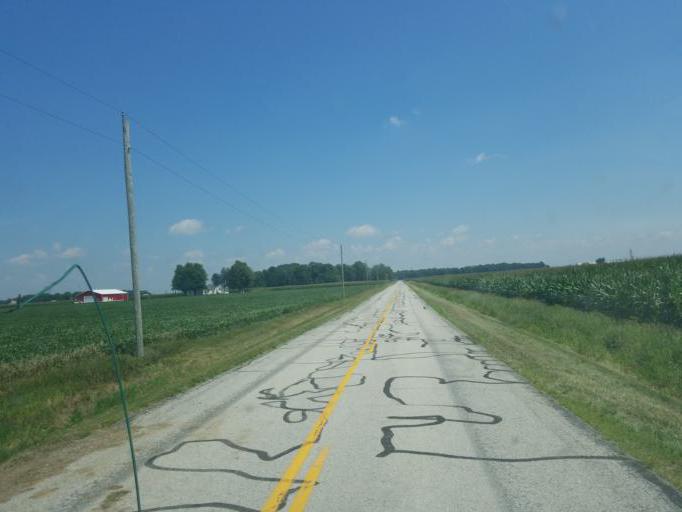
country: US
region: Ohio
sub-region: Auglaize County
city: Wapakoneta
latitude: 40.5404
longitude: -84.2480
